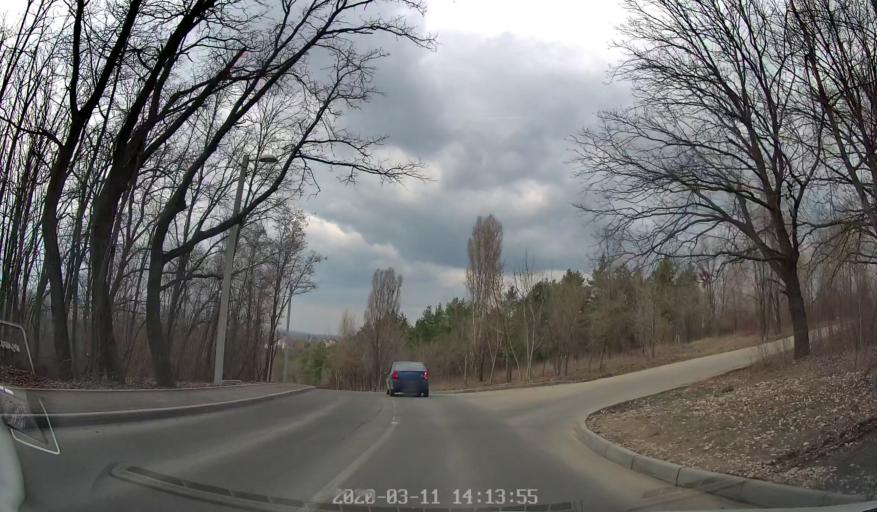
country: MD
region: Chisinau
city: Stauceni
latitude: 47.0601
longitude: 28.8862
